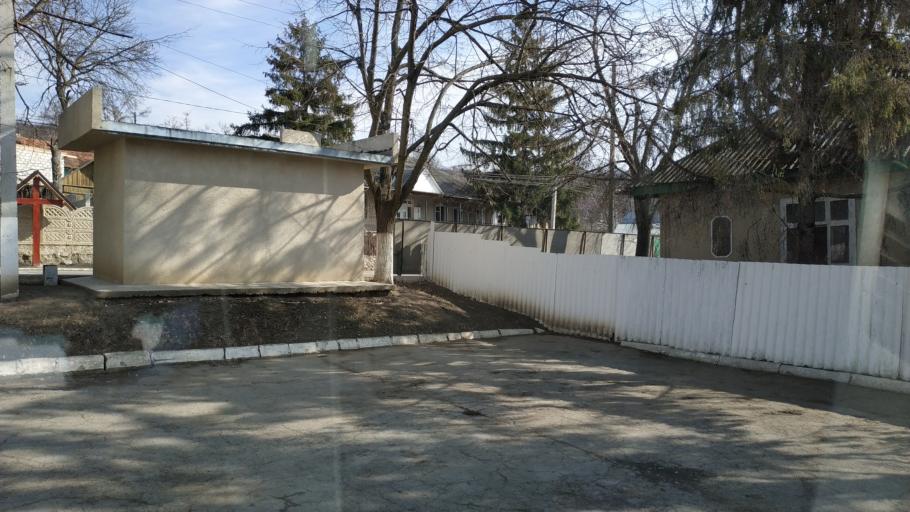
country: MD
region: Nisporeni
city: Nisporeni
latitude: 47.1772
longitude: 28.1235
